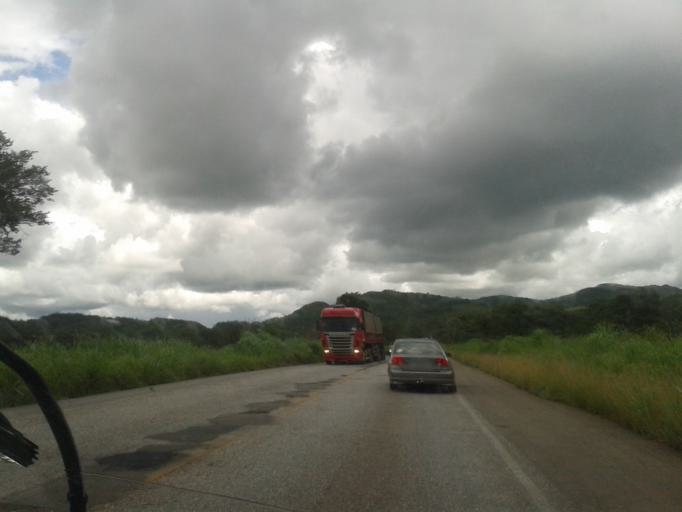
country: BR
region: Goias
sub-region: Goias
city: Goias
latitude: -15.9900
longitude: -50.0756
